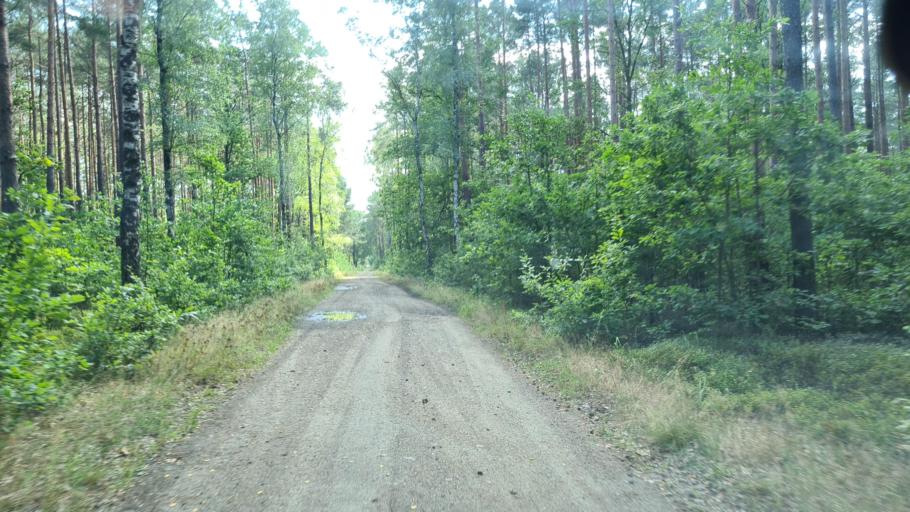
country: DE
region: Brandenburg
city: Hohenbucko
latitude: 51.7951
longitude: 13.5645
